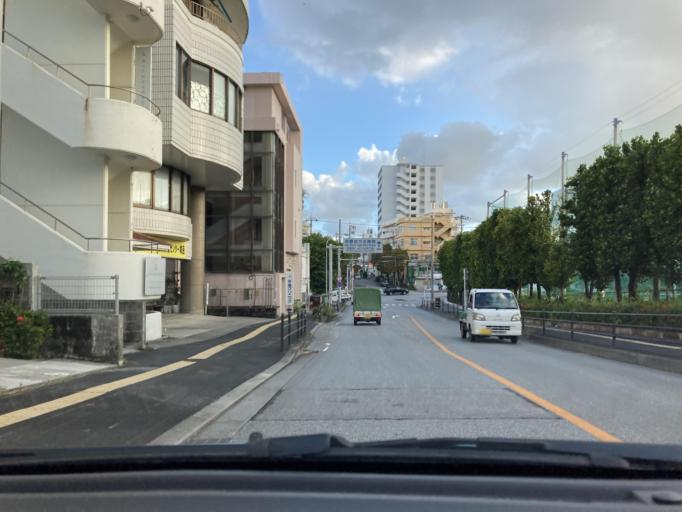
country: JP
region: Okinawa
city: Naha-shi
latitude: 26.2118
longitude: 127.6856
